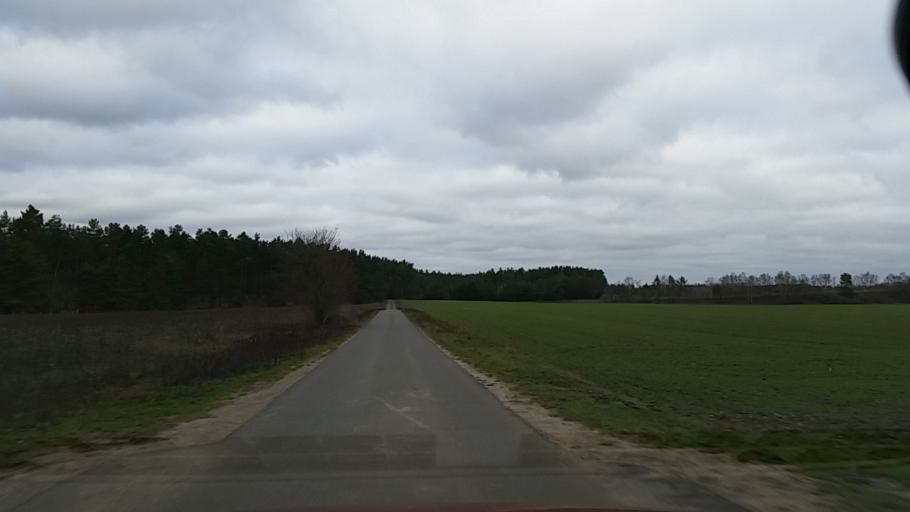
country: DE
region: Lower Saxony
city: Wieren
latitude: 52.8597
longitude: 10.6576
